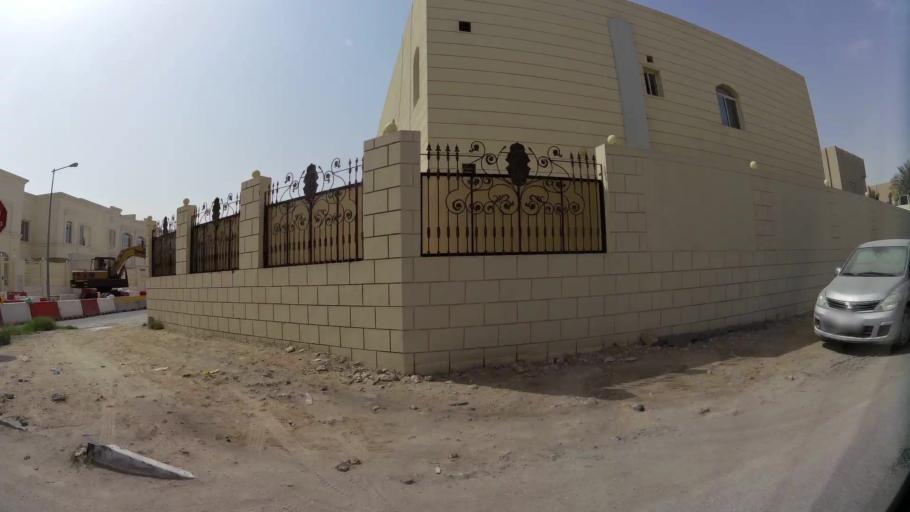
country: QA
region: Baladiyat ad Dawhah
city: Doha
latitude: 25.3050
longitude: 51.4786
